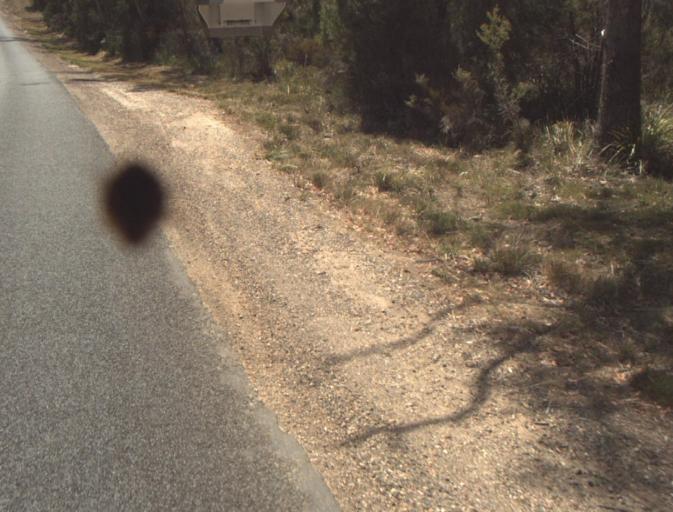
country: AU
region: Tasmania
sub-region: Launceston
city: Mayfield
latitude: -41.3053
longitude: 147.1337
